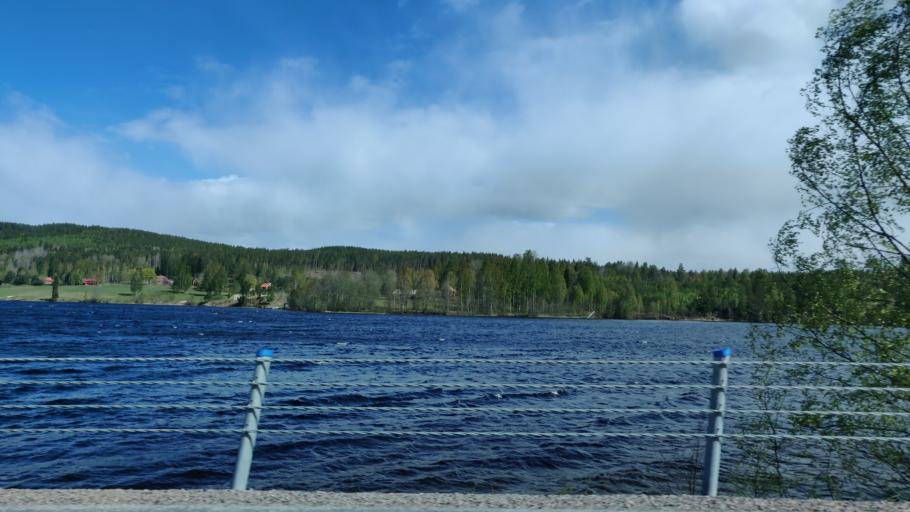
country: SE
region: Vaermland
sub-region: Hagfors Kommun
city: Hagfors
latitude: 59.8861
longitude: 13.6975
